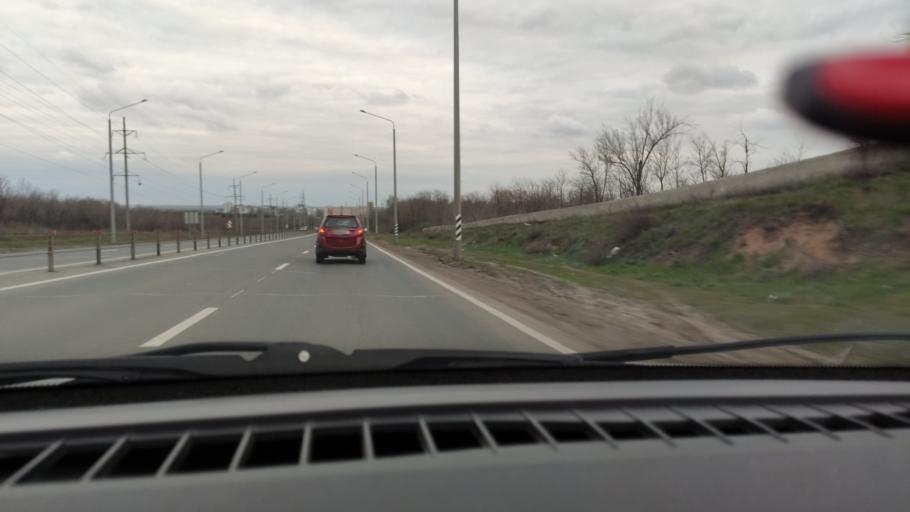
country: RU
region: Orenburg
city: Prigorodnyy
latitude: 51.7926
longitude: 55.1867
